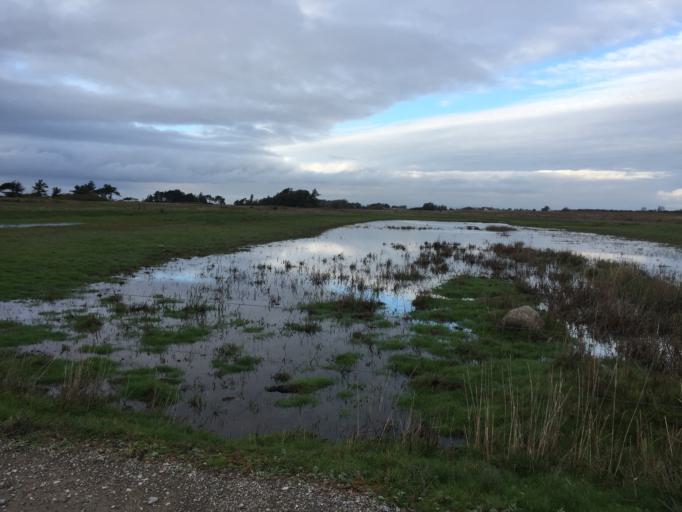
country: DK
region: Zealand
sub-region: Slagelse Kommune
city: Skaelskor
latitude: 55.2075
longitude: 11.1756
